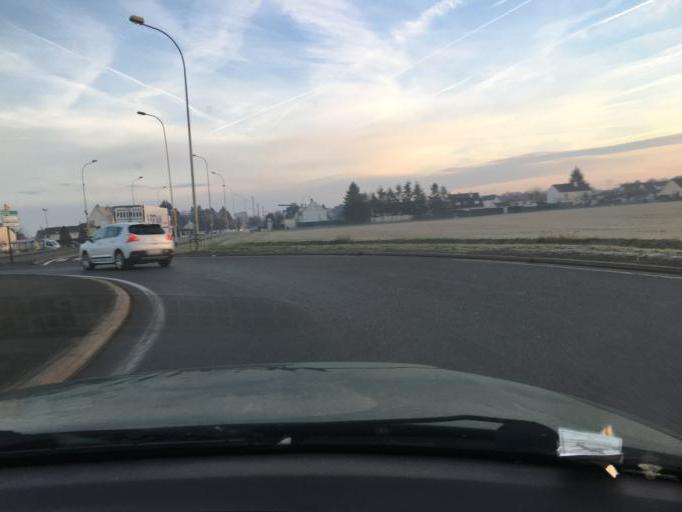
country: FR
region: Centre
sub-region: Departement du Loiret
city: Baule
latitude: 47.8207
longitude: 1.6838
